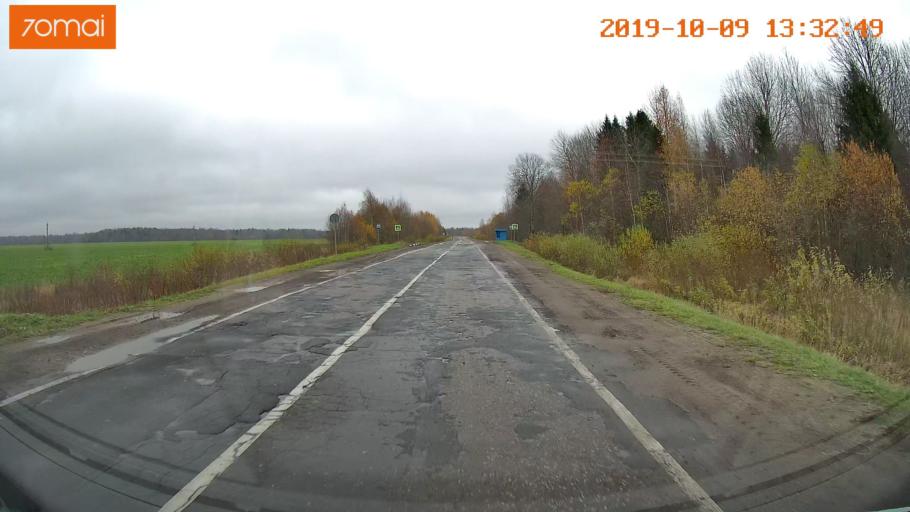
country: RU
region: Jaroslavl
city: Lyubim
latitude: 58.3245
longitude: 41.0375
